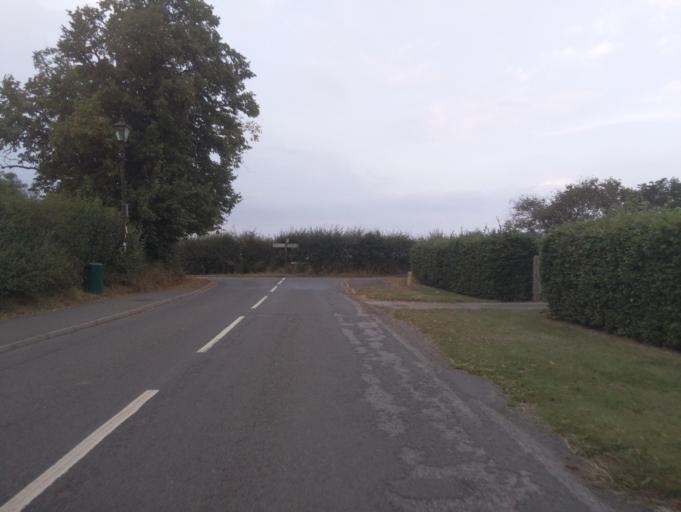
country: GB
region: England
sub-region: Lincolnshire
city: Skellingthorpe
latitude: 53.1334
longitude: -0.6382
